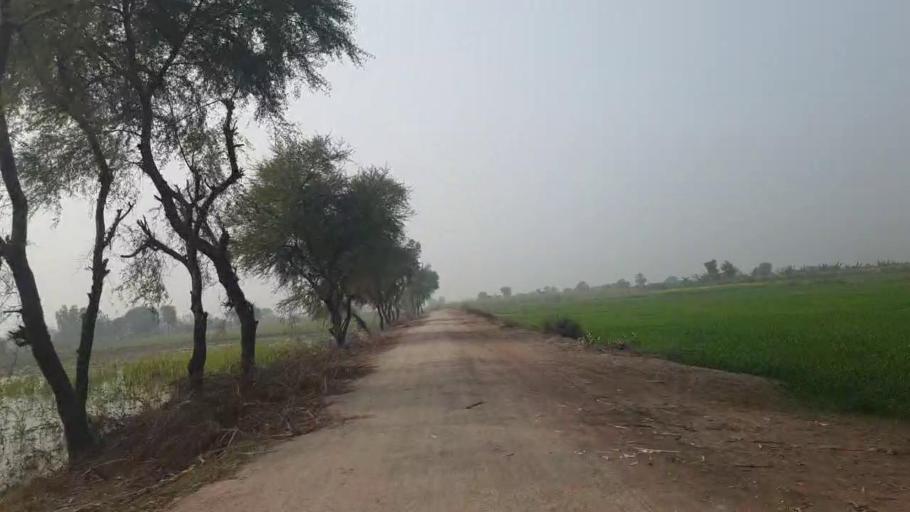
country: PK
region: Sindh
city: Tando Adam
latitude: 25.7658
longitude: 68.5744
